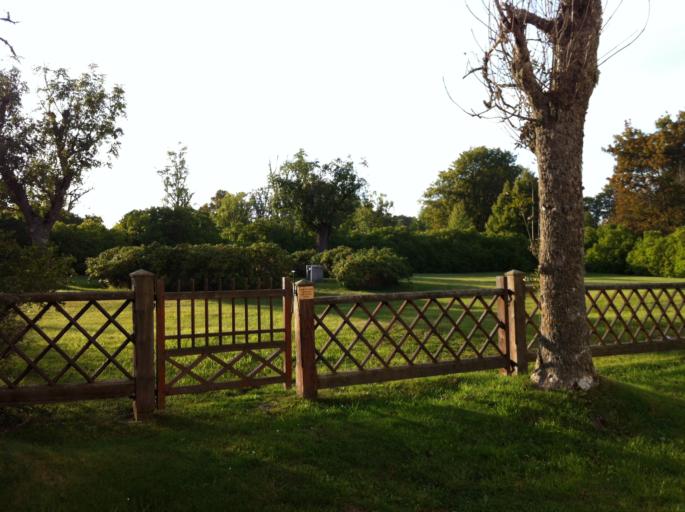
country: SE
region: Gotland
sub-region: Gotland
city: Slite
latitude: 57.4452
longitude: 18.7110
